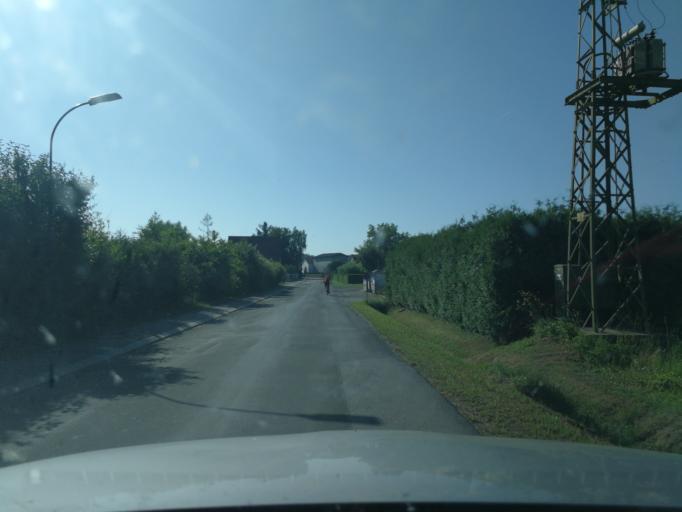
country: AT
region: Burgenland
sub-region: Politischer Bezirk Jennersdorf
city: Konigsdorf
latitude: 47.0058
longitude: 16.1650
